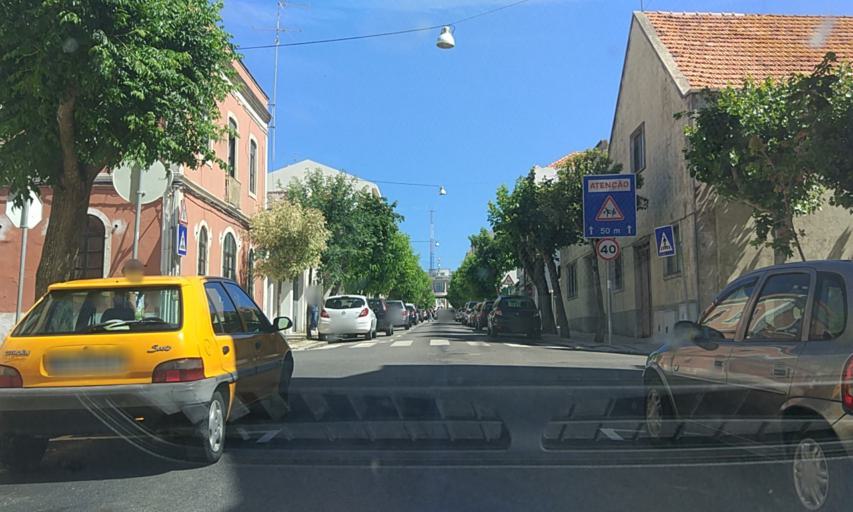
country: PT
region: Coimbra
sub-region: Figueira da Foz
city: Figueira da Foz
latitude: 40.1496
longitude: -8.8503
